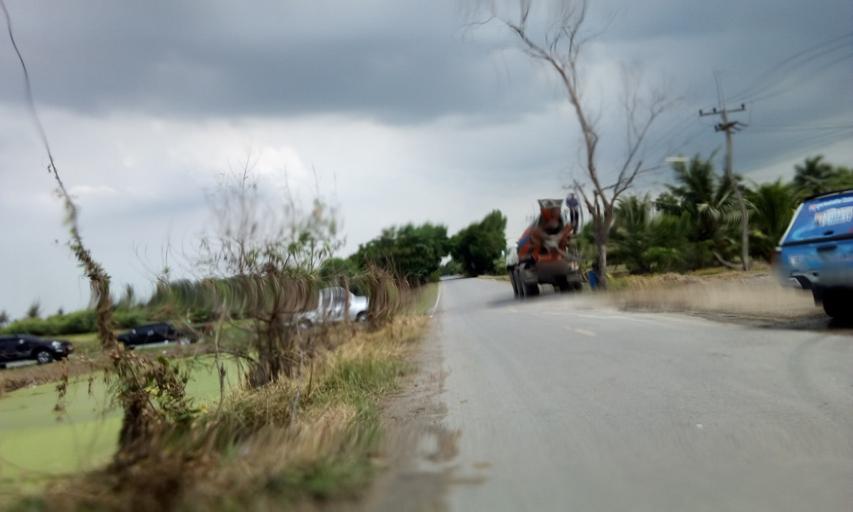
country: TH
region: Pathum Thani
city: Ban Lam Luk Ka
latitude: 14.0220
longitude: 100.8468
